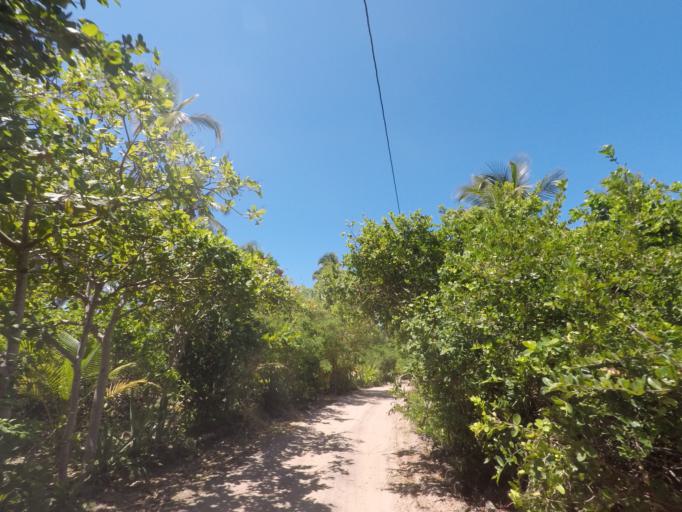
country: BR
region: Bahia
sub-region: Marau
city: Marau
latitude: -13.9975
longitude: -38.9444
